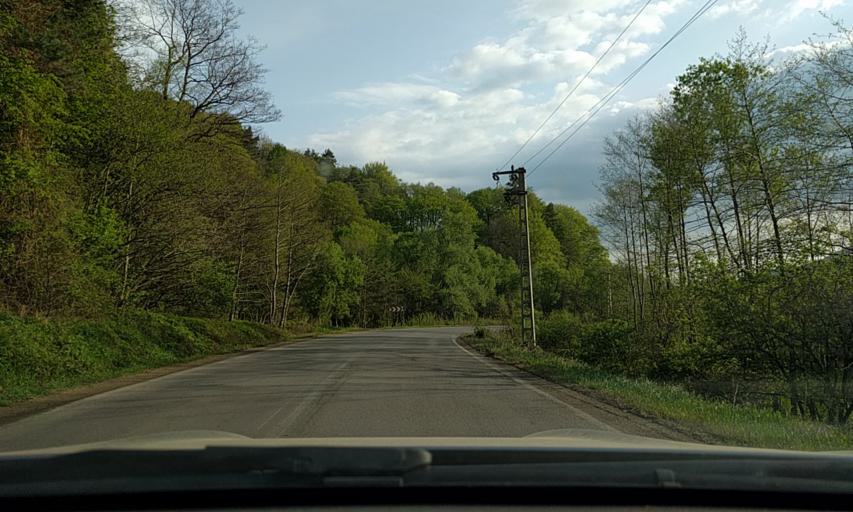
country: RO
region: Bacau
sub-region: Oras Slanic-Moldova
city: Slanic-Moldova
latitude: 46.1256
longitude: 26.4373
